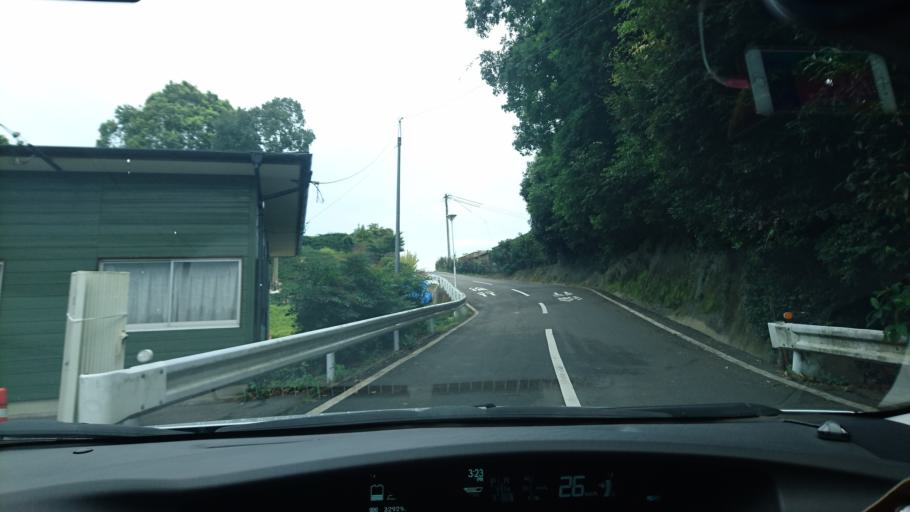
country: JP
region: Saga Prefecture
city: Takeocho-takeo
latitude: 33.2213
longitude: 130.0741
